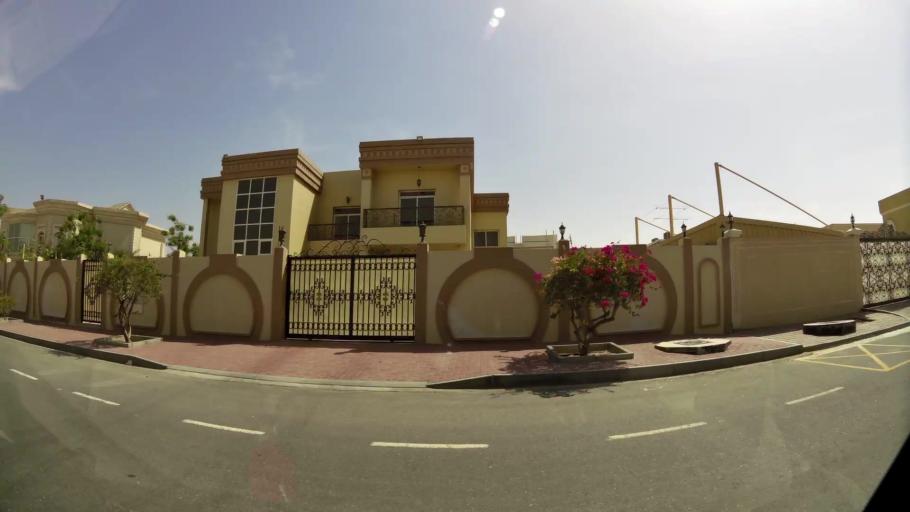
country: AE
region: Ash Shariqah
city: Sharjah
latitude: 25.2031
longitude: 55.4260
